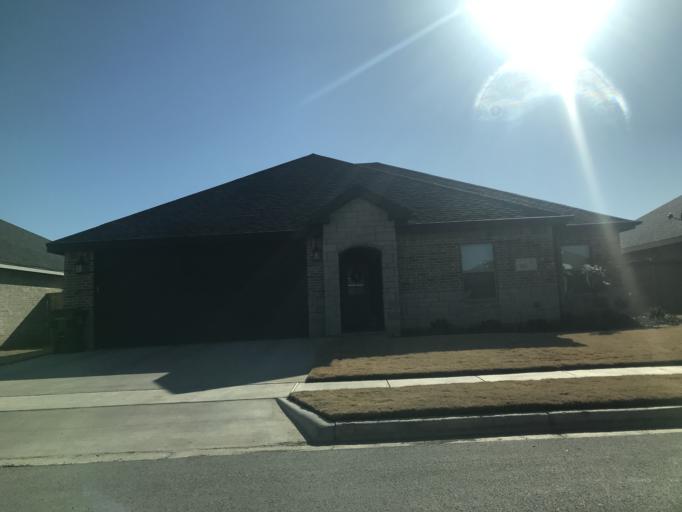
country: US
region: Texas
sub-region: Taylor County
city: Potosi
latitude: 32.3717
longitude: -99.7196
